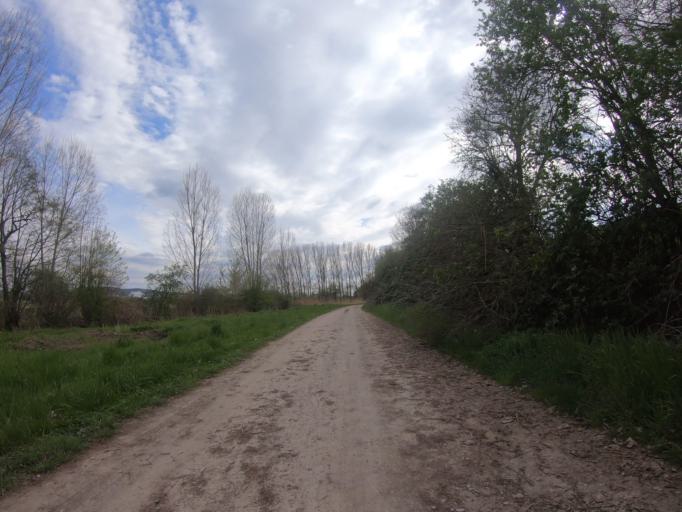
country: DE
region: Lower Saxony
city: Nordstemmen
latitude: 52.1828
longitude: 9.7772
